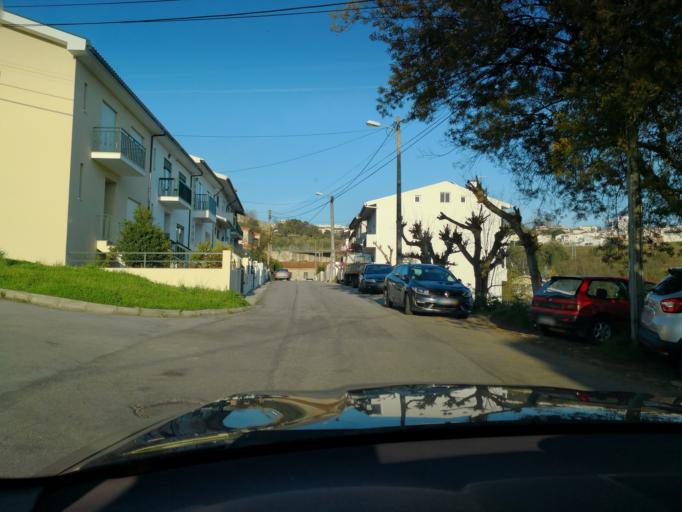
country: PT
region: Vila Real
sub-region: Vila Real
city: Vila Real
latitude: 41.3045
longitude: -7.7567
